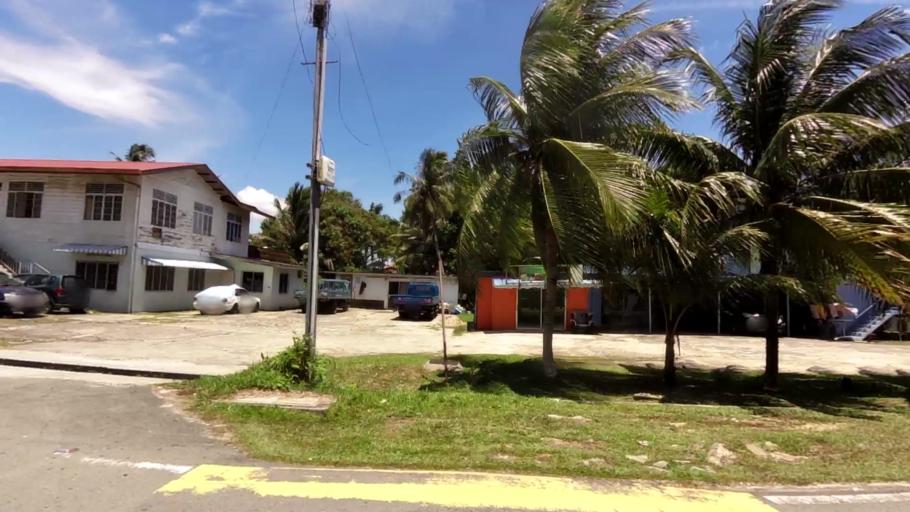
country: BN
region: Brunei and Muara
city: Bandar Seri Begawan
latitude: 4.9286
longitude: 114.9314
